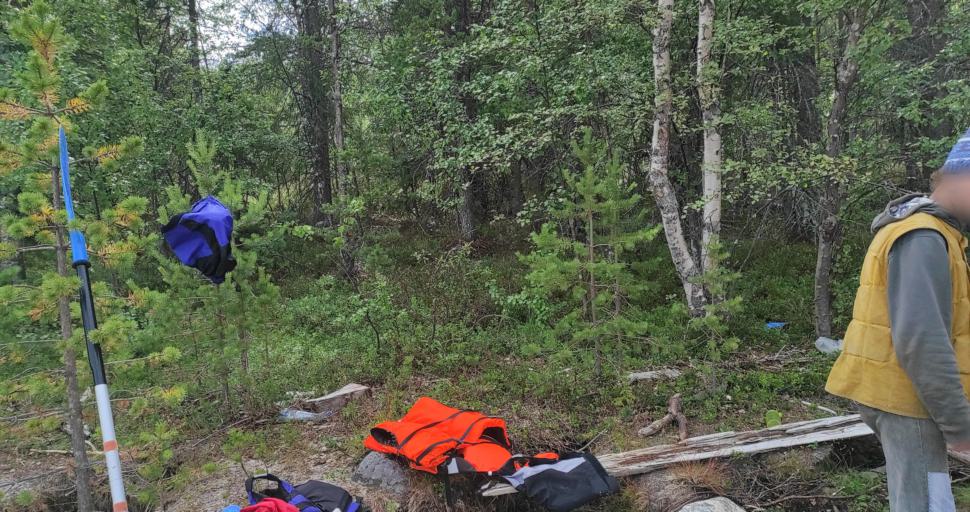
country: RU
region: Murmansk
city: Zelenoborskiy
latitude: 66.8725
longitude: 32.4977
